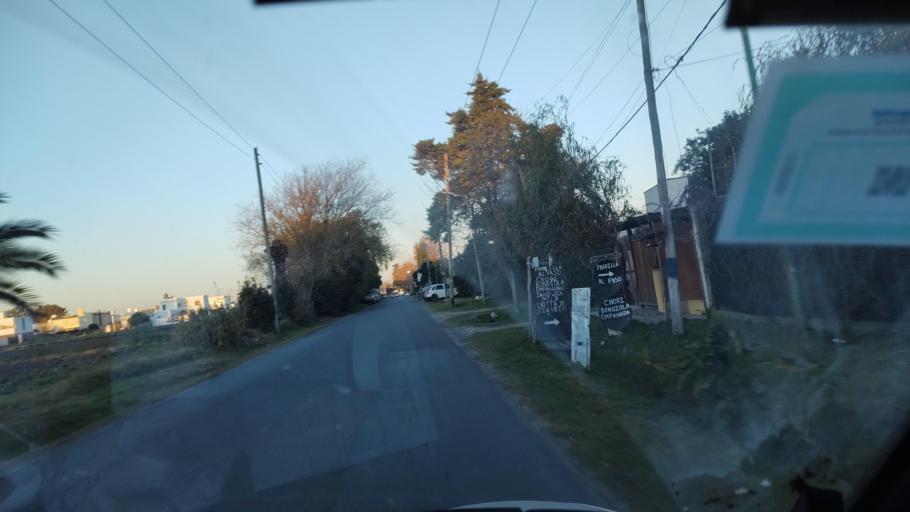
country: AR
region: Buenos Aires
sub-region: Partido de La Plata
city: La Plata
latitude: -34.9059
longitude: -58.0373
